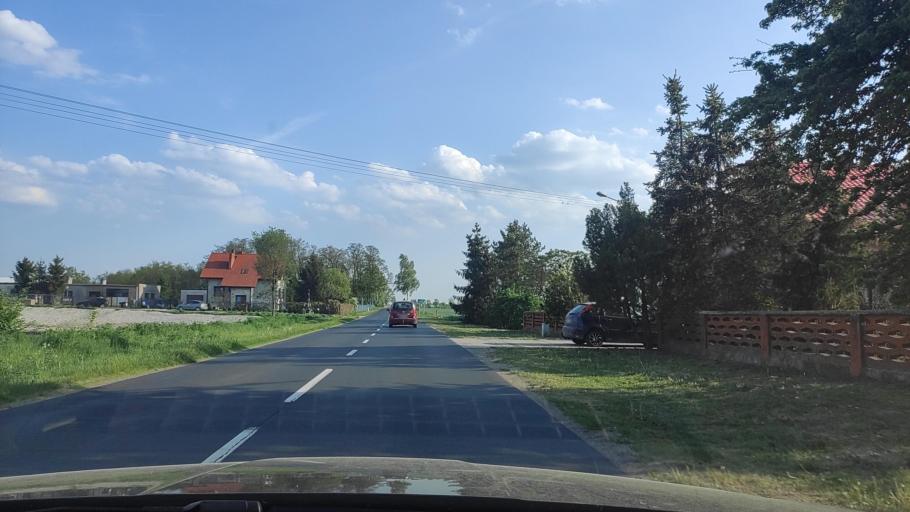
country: PL
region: Greater Poland Voivodeship
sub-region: Powiat poznanski
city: Kleszczewo
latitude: 52.3484
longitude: 17.1711
